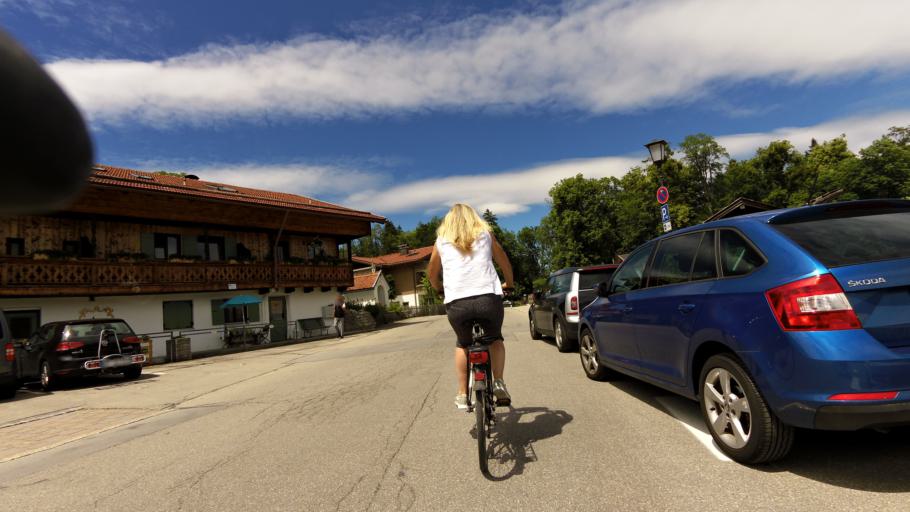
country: DE
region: Bavaria
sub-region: Upper Bavaria
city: Tegernsee
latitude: 47.7035
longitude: 11.7371
